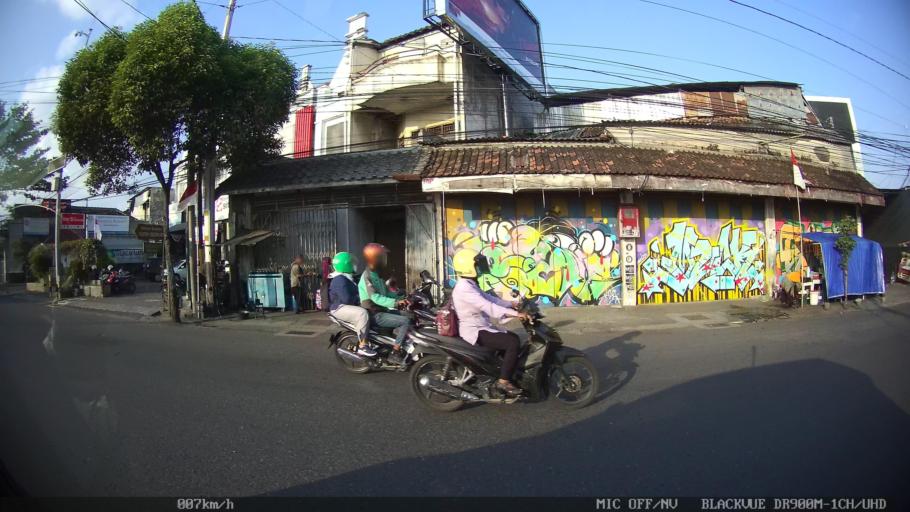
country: ID
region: Daerah Istimewa Yogyakarta
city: Yogyakarta
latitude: -7.8039
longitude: 110.3700
